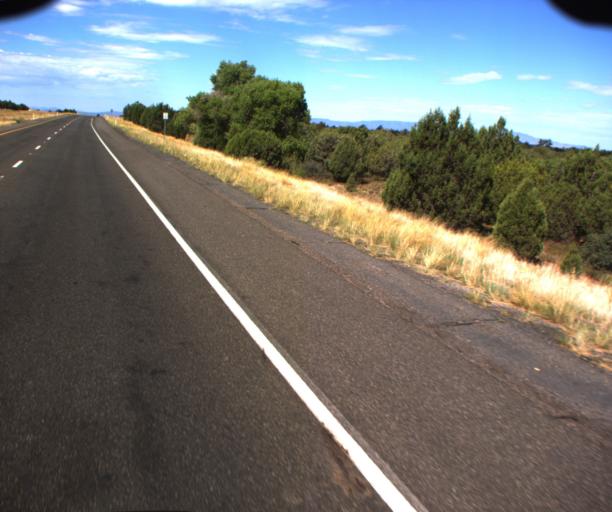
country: US
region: Arizona
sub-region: Yavapai County
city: Village of Oak Creek (Big Park)
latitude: 34.7607
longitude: -111.6614
